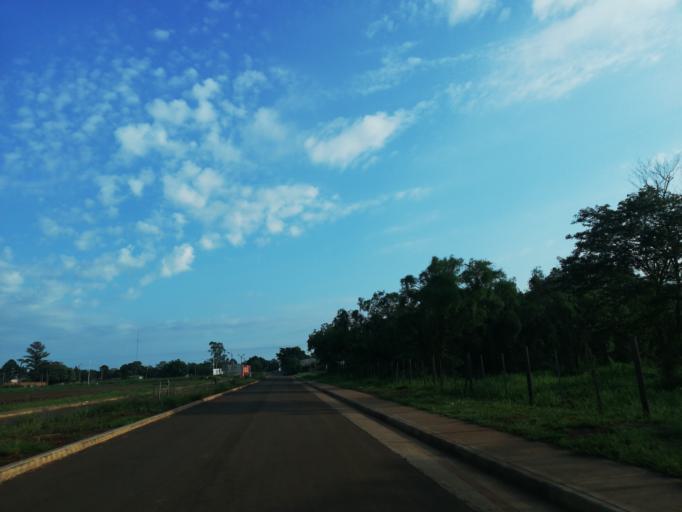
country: AR
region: Misiones
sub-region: Departamento de Capital
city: Posadas
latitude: -27.3934
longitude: -55.9239
